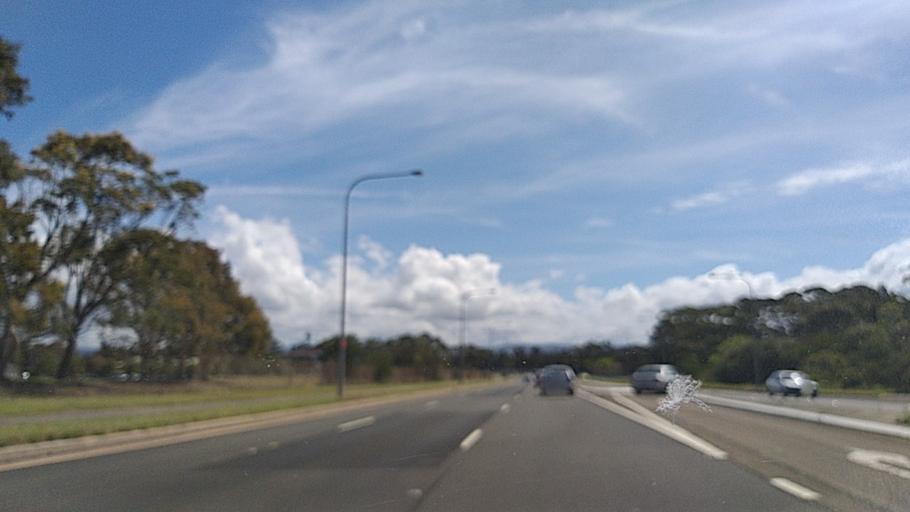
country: AU
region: New South Wales
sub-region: Wollongong
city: Lake Heights
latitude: -34.5070
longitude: 150.8809
